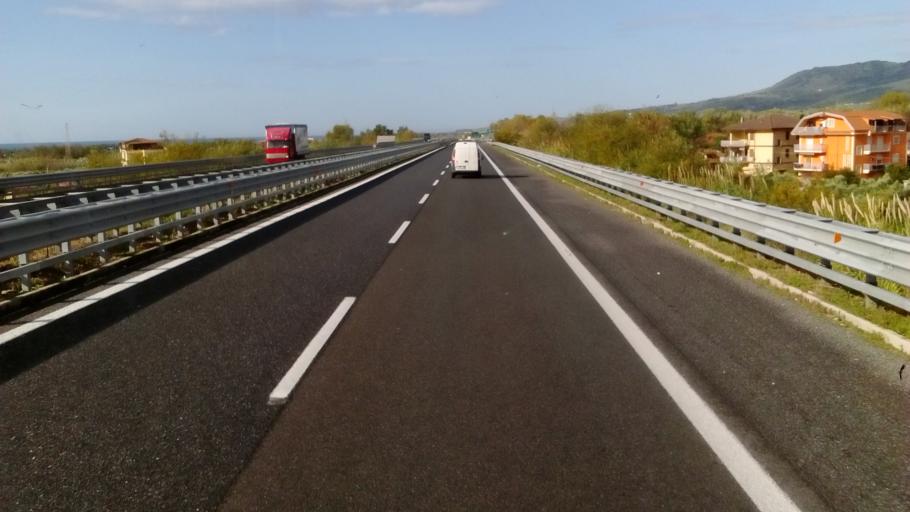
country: IT
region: Calabria
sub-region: Provincia di Catanzaro
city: Santa Eufemia Lamezia
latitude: 38.9269
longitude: 16.2477
